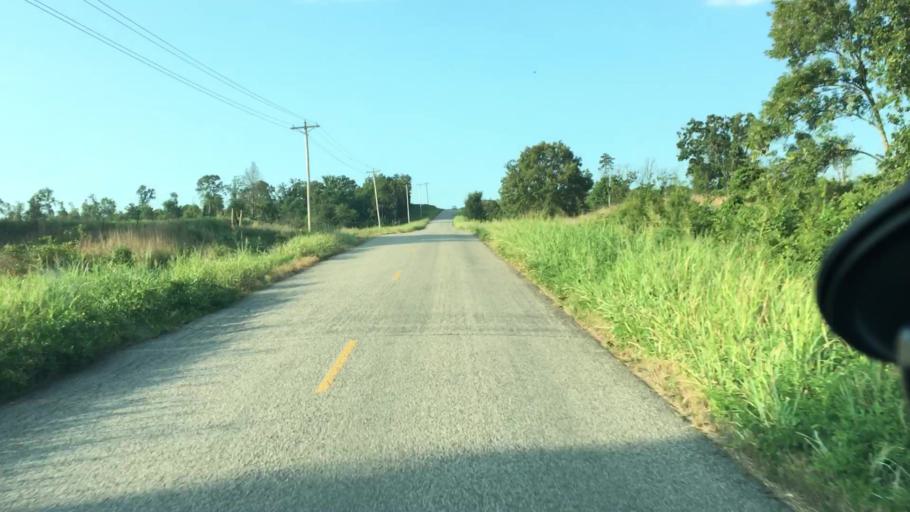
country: US
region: Arkansas
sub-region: Johnson County
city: Coal Hill
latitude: 35.3611
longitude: -93.6131
